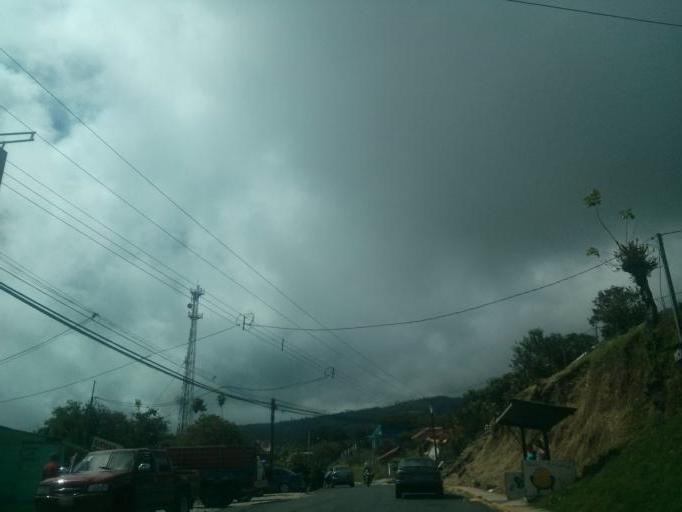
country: CR
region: Cartago
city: Turrialba
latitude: 9.9659
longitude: -83.7303
